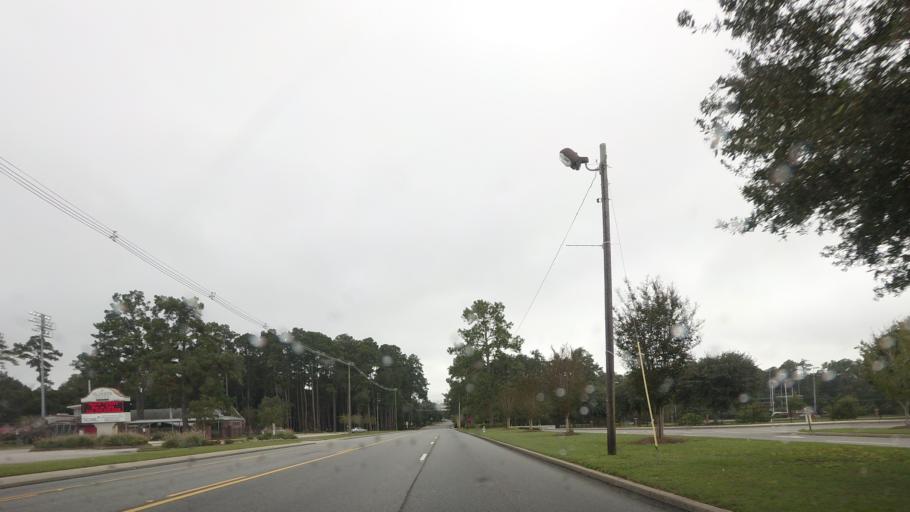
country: US
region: Georgia
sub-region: Lowndes County
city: Remerton
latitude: 30.8667
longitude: -83.2897
